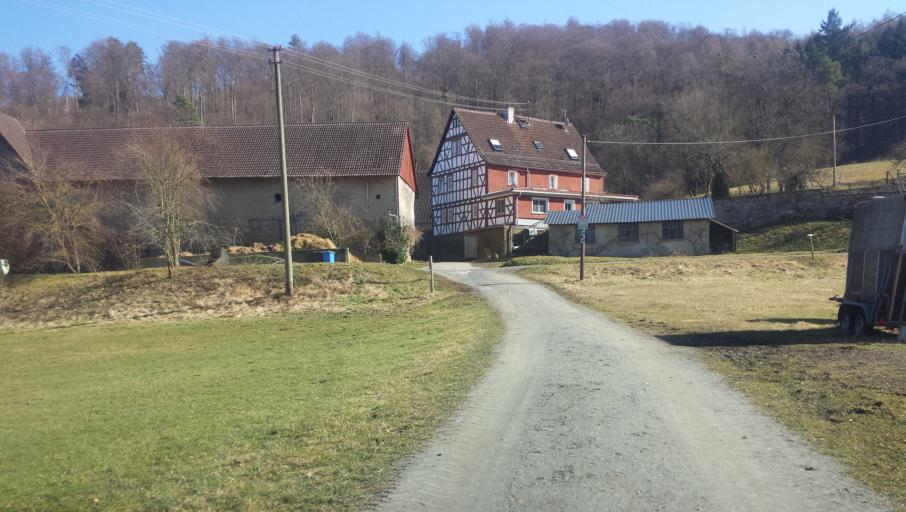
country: DE
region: Hesse
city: Lutzelbach
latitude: 49.7622
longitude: 8.7807
